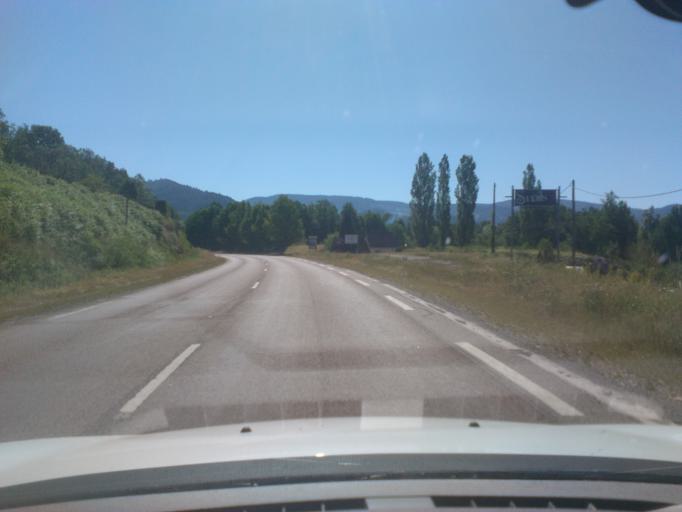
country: FR
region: Lorraine
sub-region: Departement des Vosges
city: Le Syndicat
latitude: 48.0248
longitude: 6.6936
